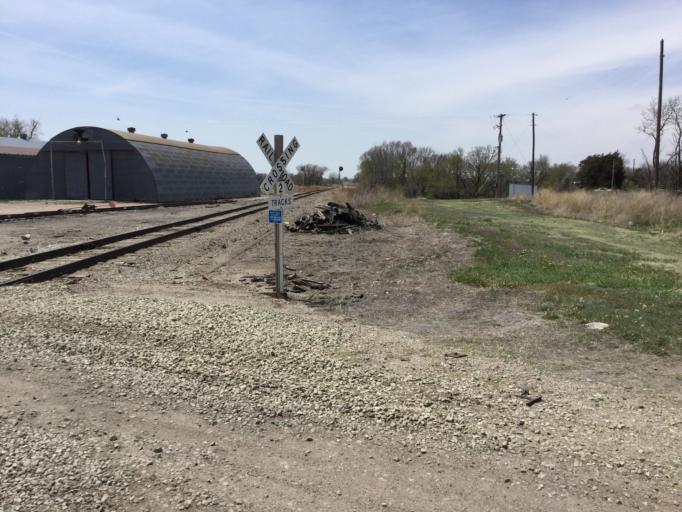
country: US
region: Kansas
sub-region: Norton County
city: Norton
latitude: 39.7387
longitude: -100.1776
